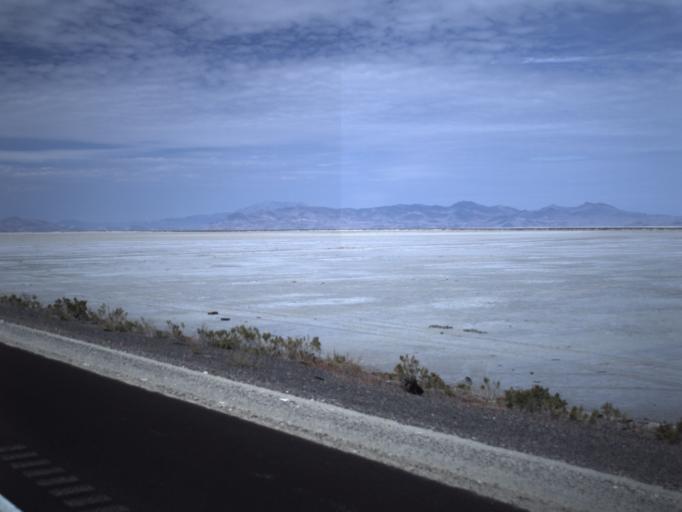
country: US
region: Utah
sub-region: Tooele County
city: Wendover
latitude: 40.7321
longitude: -113.5133
